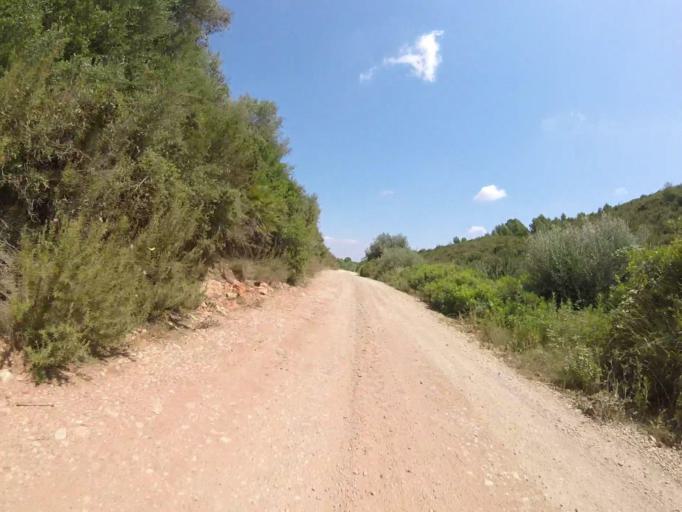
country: ES
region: Valencia
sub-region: Provincia de Castello
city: Torreblanca
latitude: 40.2276
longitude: 0.1570
